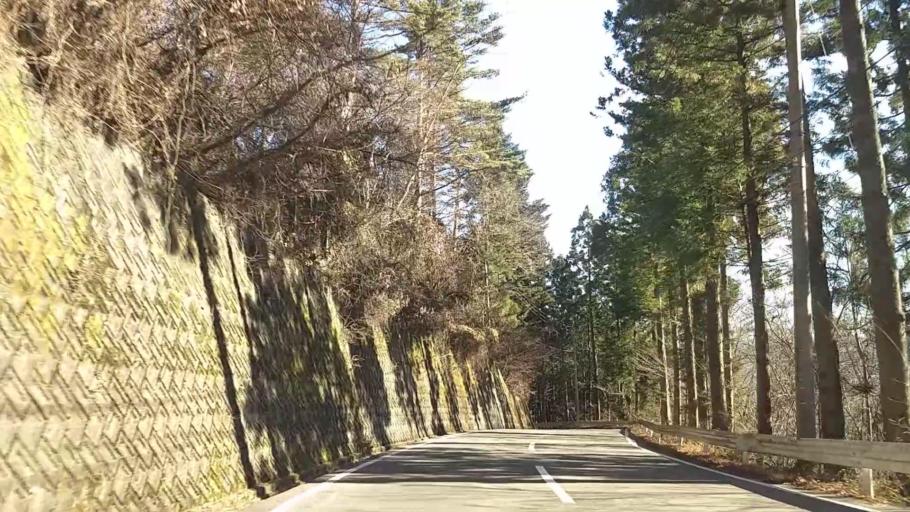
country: JP
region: Yamanashi
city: Otsuki
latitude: 35.5132
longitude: 138.9817
